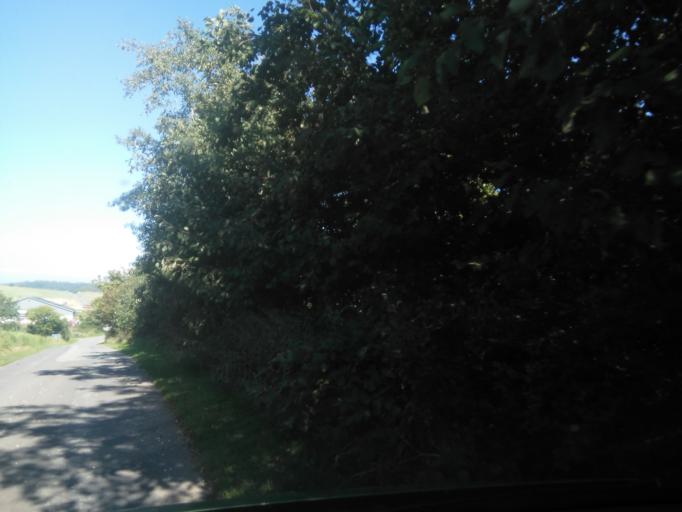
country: DK
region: Central Jutland
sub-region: Syddjurs Kommune
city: Ronde
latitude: 56.1775
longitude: 10.4219
